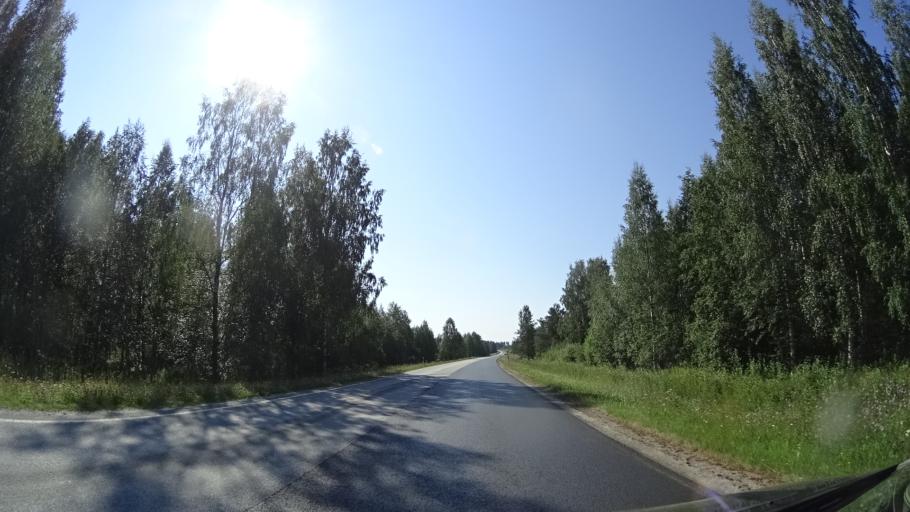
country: FI
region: North Karelia
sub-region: Joensuu
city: Juuka
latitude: 63.2382
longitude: 29.2819
